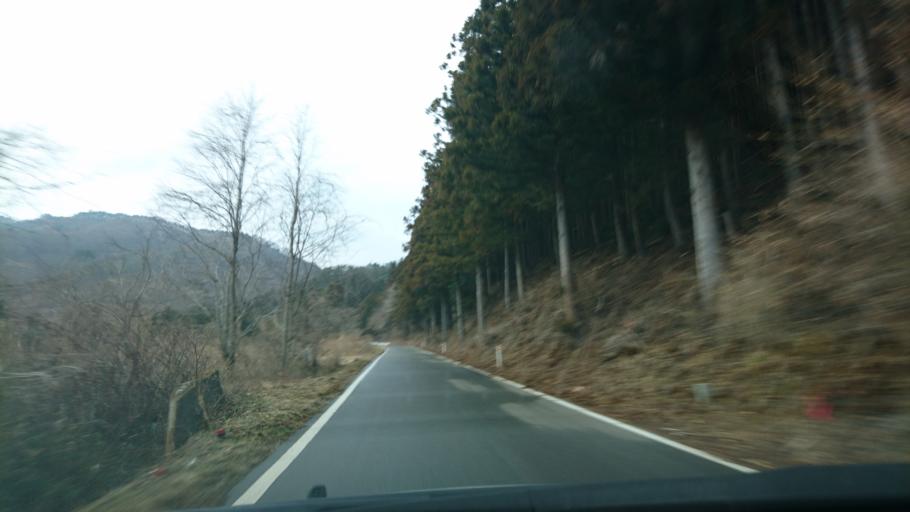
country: JP
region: Iwate
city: Ofunato
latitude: 38.9899
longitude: 141.5519
